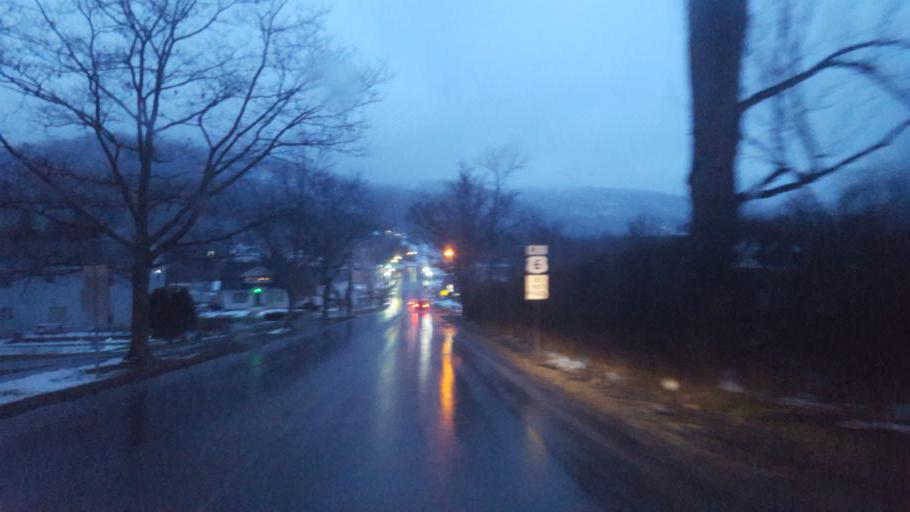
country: US
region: Pennsylvania
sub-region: McKean County
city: Smethport
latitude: 41.8094
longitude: -78.4516
